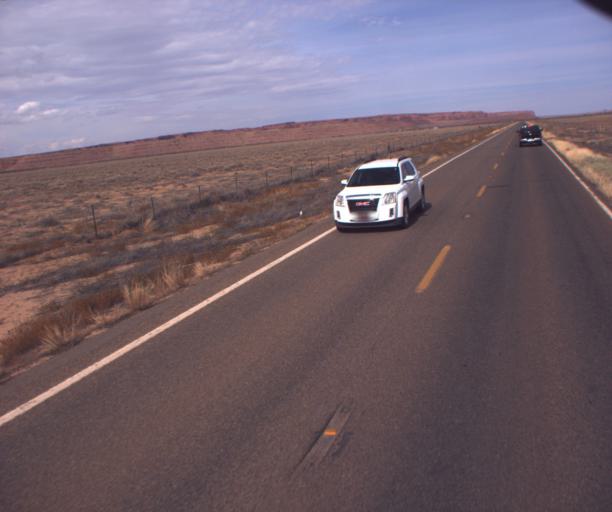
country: US
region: Arizona
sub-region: Apache County
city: Many Farms
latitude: 36.4459
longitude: -109.6075
